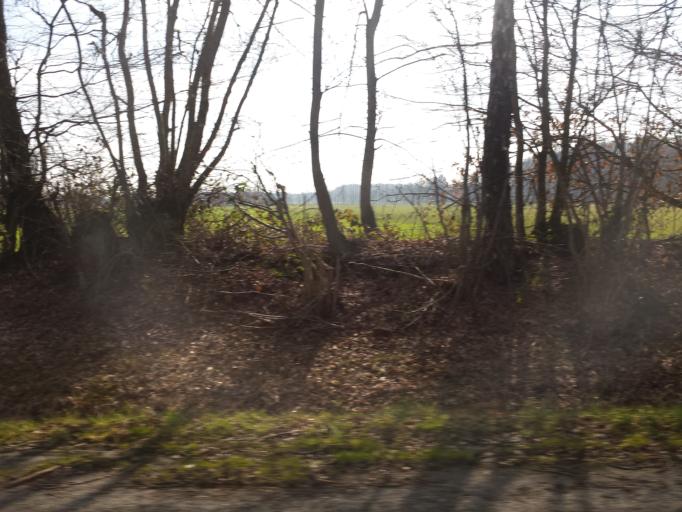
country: DE
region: North Rhine-Westphalia
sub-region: Regierungsbezirk Munster
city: Havixbeck
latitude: 51.9528
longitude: 7.5116
